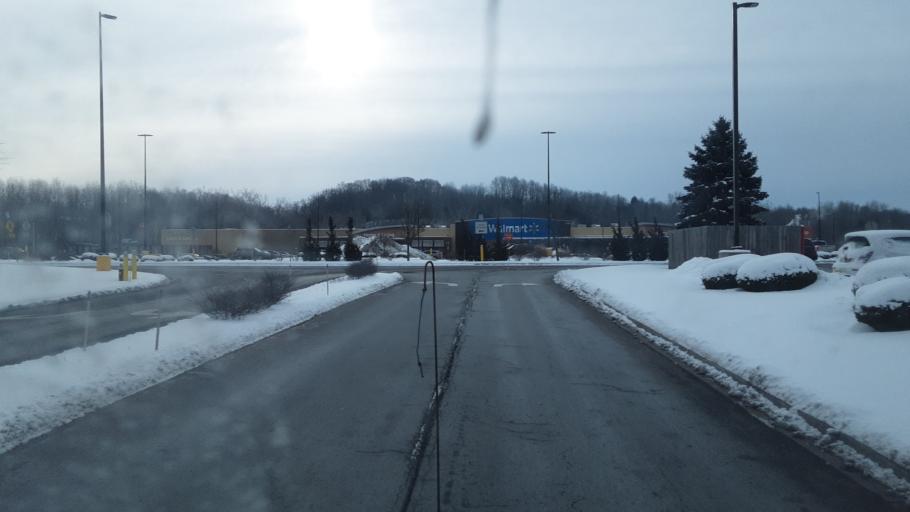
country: US
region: New York
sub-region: Wayne County
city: Newark
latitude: 43.0532
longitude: -77.0592
